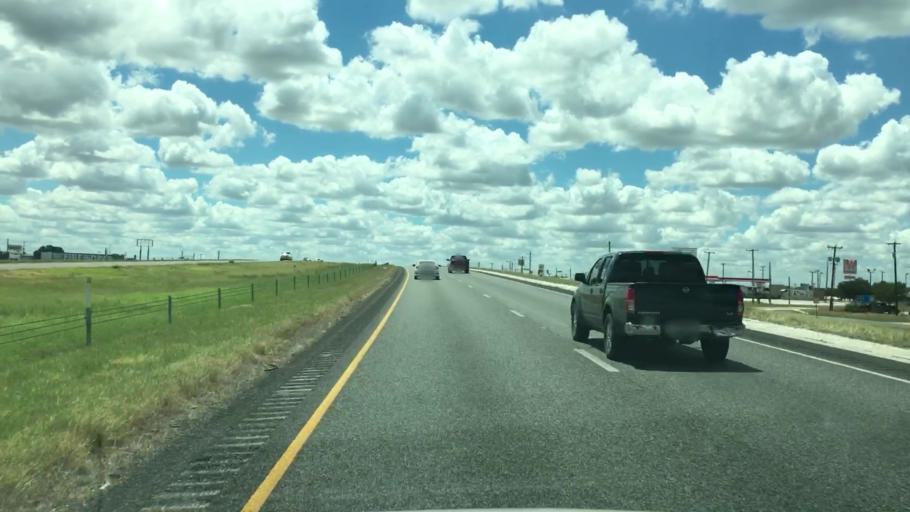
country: US
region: Texas
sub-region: Bexar County
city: Elmendorf
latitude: 29.2209
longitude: -98.4114
